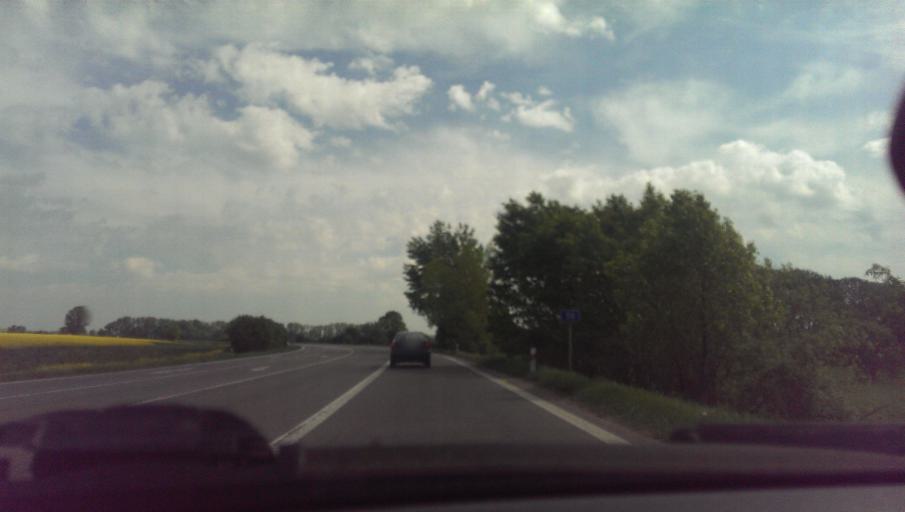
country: CZ
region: Zlin
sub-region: Okres Uherske Hradiste
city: Stare Mesto
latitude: 49.0899
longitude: 17.4488
